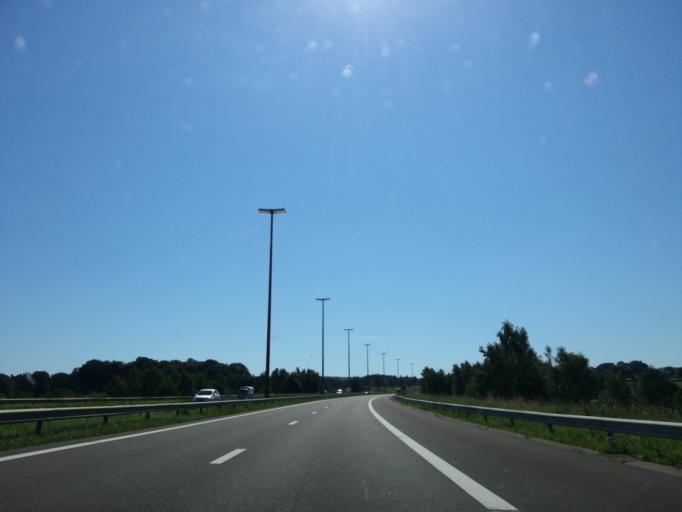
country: BE
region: Wallonia
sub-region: Province de Liege
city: Jalhay
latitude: 50.5226
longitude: 5.9369
